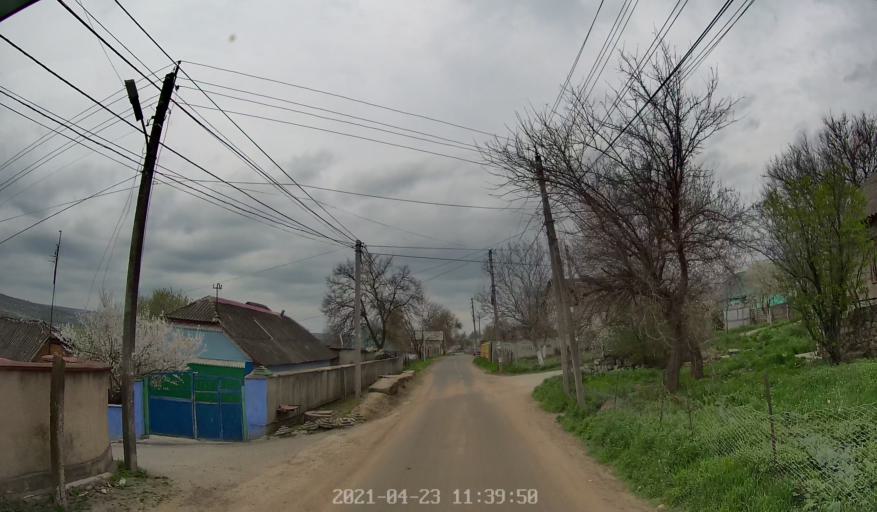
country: MD
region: Chisinau
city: Vadul lui Voda
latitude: 47.1180
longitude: 29.0517
